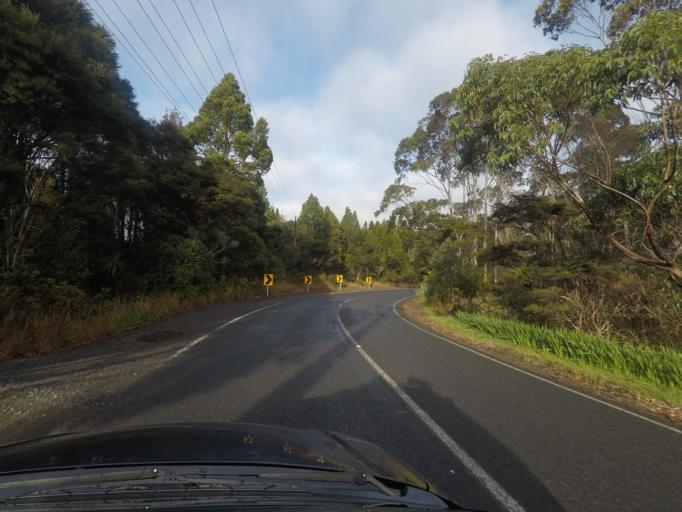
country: NZ
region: Auckland
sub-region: Auckland
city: Waitakere
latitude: -36.9133
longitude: 174.6052
